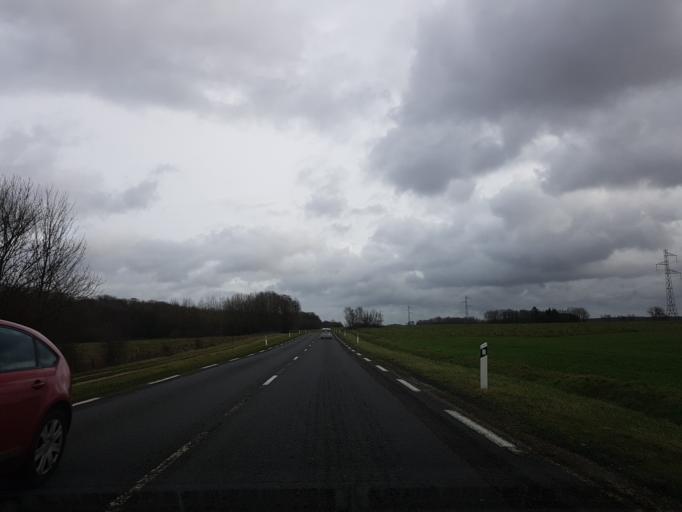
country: FR
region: Champagne-Ardenne
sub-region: Departement de la Haute-Marne
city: Chalindrey
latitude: 47.8137
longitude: 5.5113
